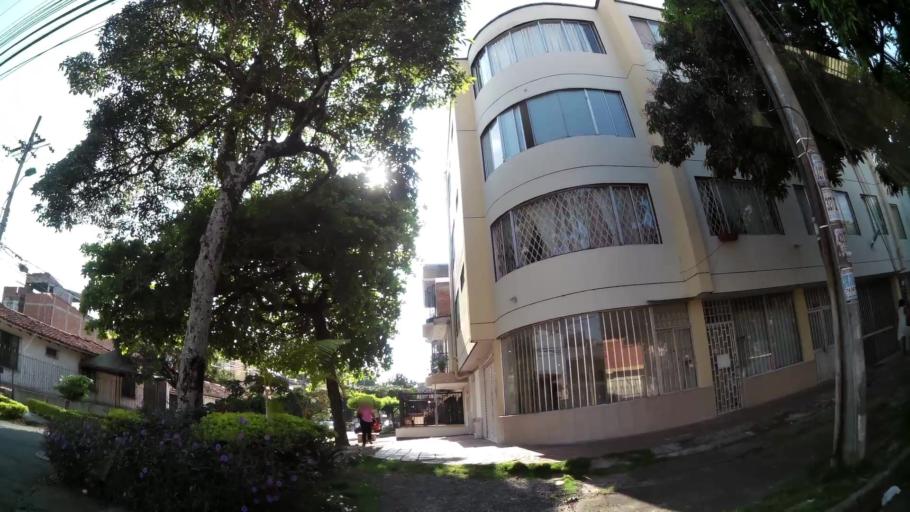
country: CO
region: Valle del Cauca
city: Cali
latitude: 3.4190
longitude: -76.5345
